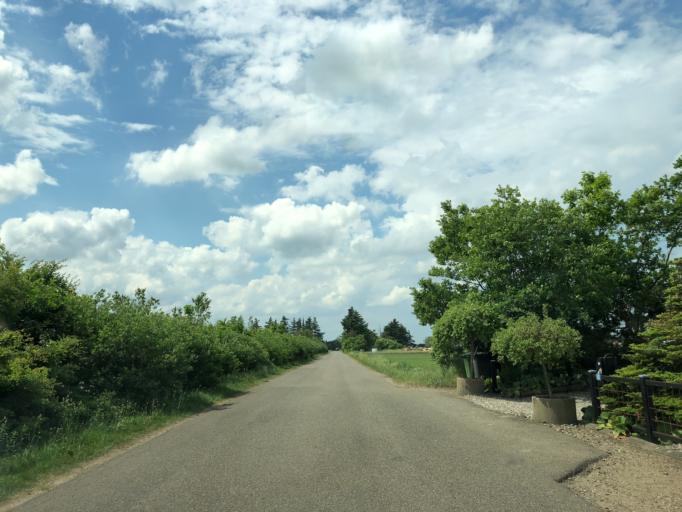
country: DK
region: Central Jutland
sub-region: Holstebro Kommune
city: Ulfborg
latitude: 56.3479
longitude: 8.3296
